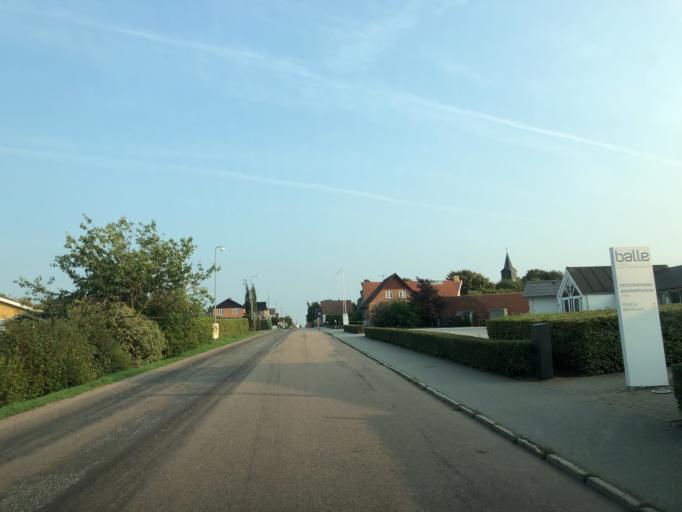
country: DK
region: South Denmark
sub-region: Vejle Kommune
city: Jelling
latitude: 55.7113
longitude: 9.3739
